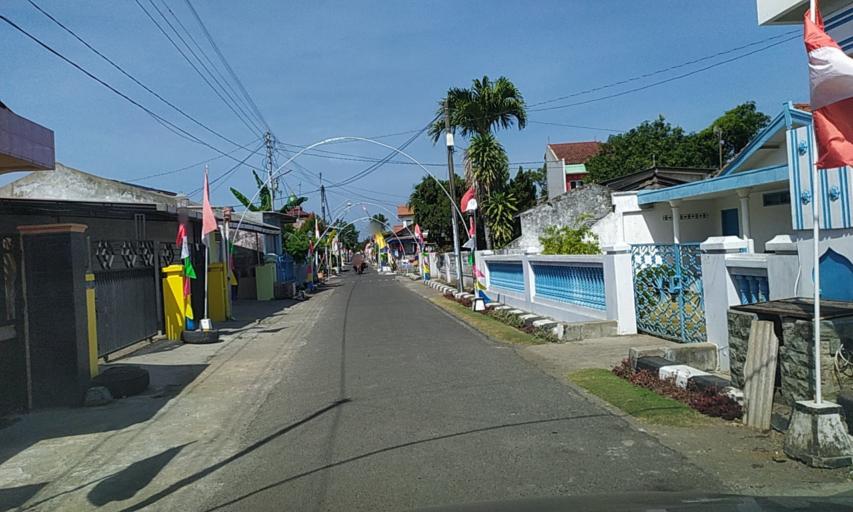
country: ID
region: Central Java
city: Karangbadar Kidul
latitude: -7.7152
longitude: 109.0076
